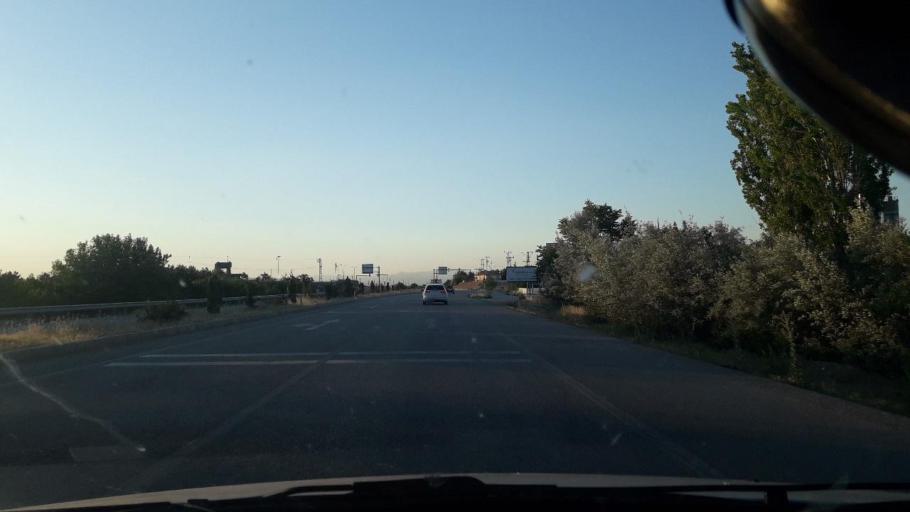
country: TR
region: Malatya
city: Yesilyurt
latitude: 38.3492
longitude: 38.2327
